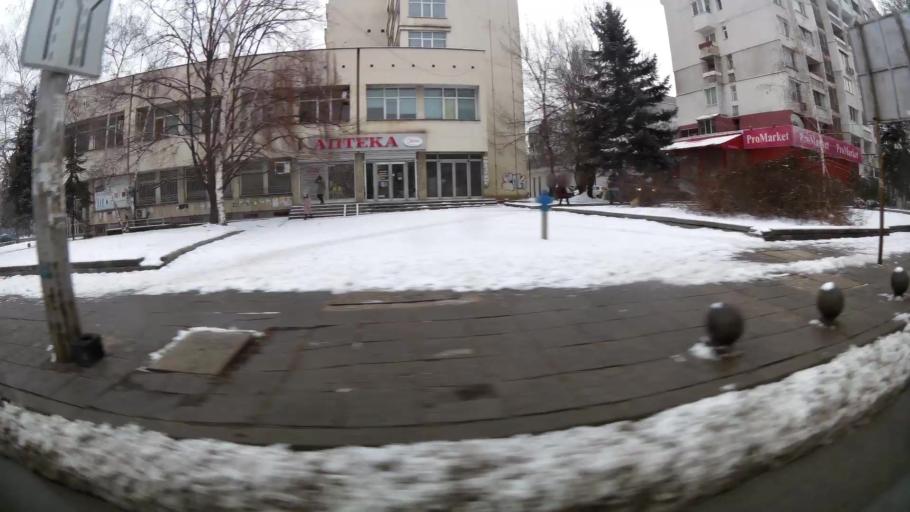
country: BG
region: Sofia-Capital
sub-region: Stolichna Obshtina
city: Sofia
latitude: 42.7123
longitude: 23.3151
